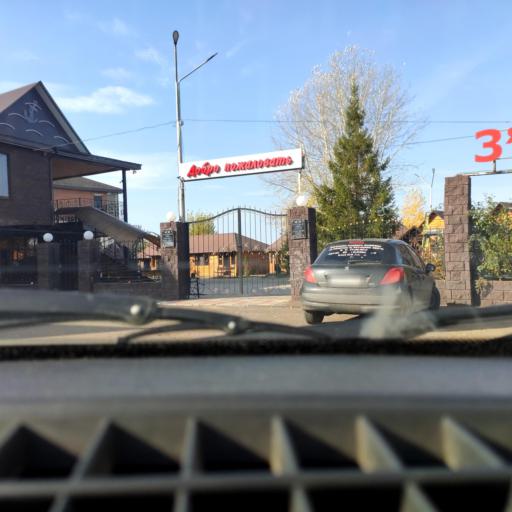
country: RU
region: Bashkortostan
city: Ufa
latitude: 54.6888
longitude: 55.9591
